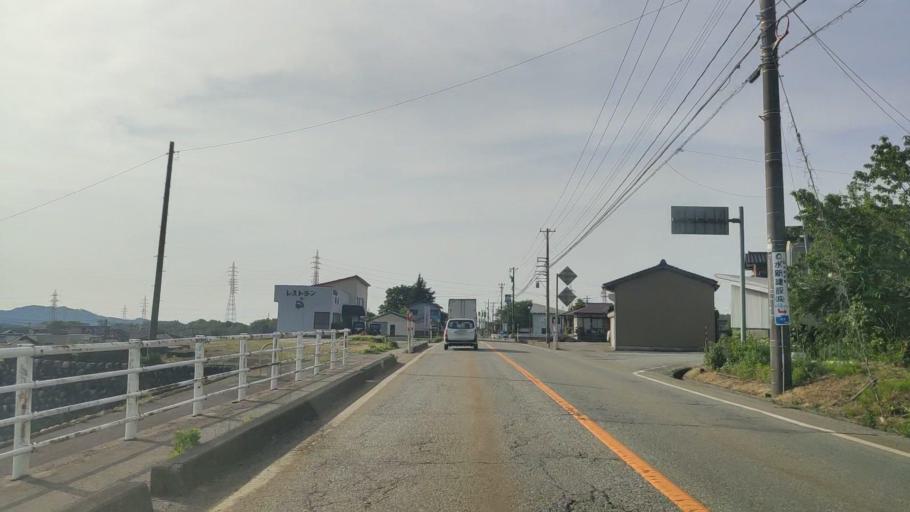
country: JP
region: Toyama
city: Yatsuomachi-higashikumisaka
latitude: 36.5619
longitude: 137.2142
